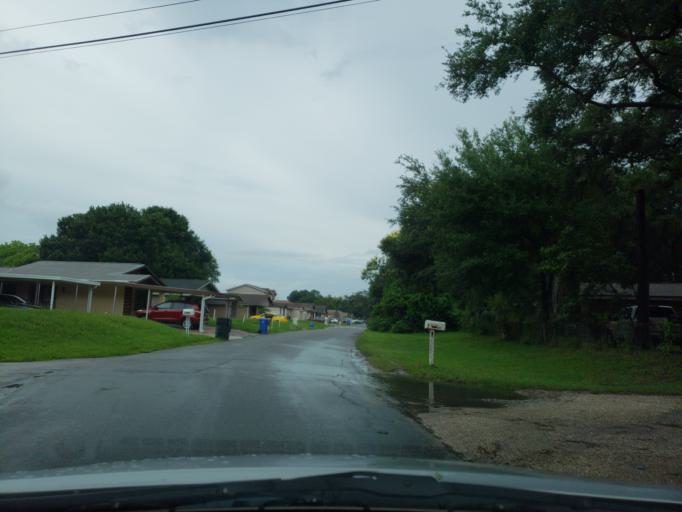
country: US
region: Florida
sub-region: Hillsborough County
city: Egypt Lake-Leto
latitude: 28.0034
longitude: -82.5091
